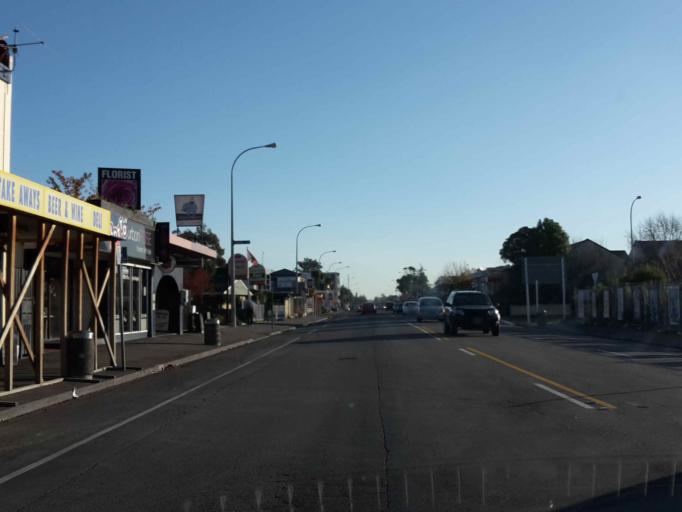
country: NZ
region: Canterbury
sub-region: Christchurch City
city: Christchurch
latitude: -43.5289
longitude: 172.6114
